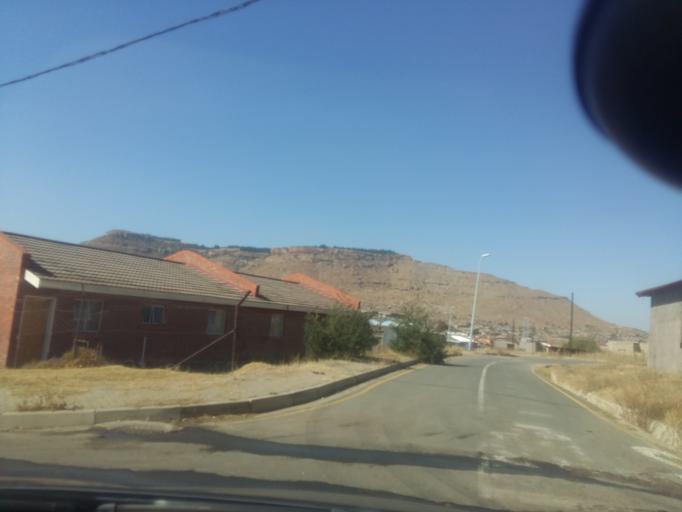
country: LS
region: Maseru
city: Maseru
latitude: -29.3396
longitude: 27.4531
